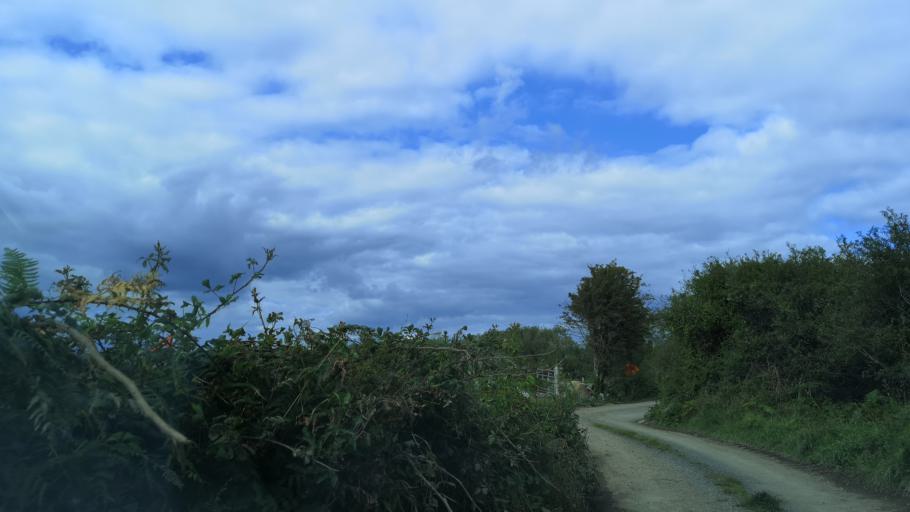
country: IE
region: Connaught
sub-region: County Galway
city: Moycullen
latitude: 53.3197
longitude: -9.1329
